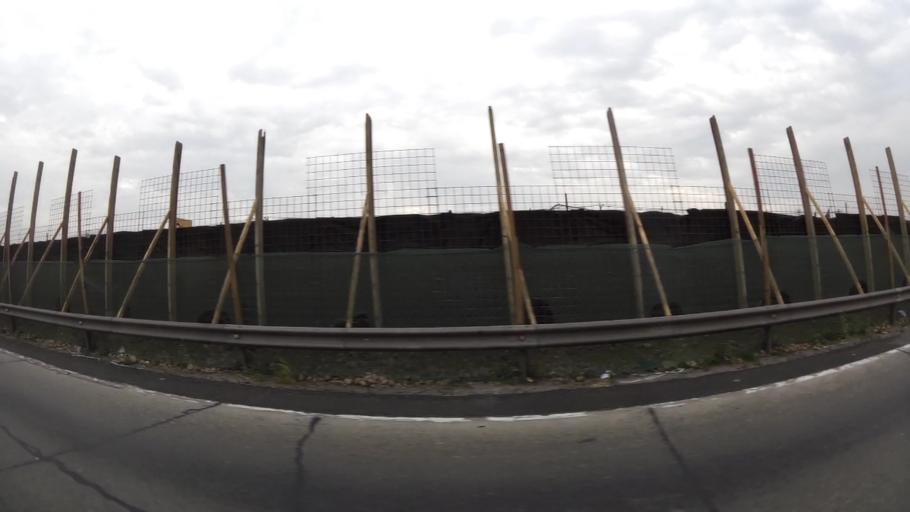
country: CL
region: Santiago Metropolitan
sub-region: Provincia de Chacabuco
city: Chicureo Abajo
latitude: -33.3498
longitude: -70.7075
